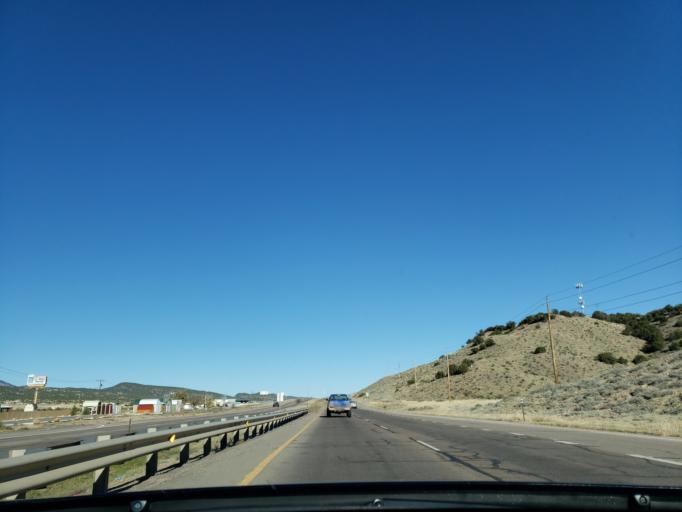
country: US
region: Colorado
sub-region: Fremont County
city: Lincoln Park
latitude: 38.4479
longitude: -105.1747
